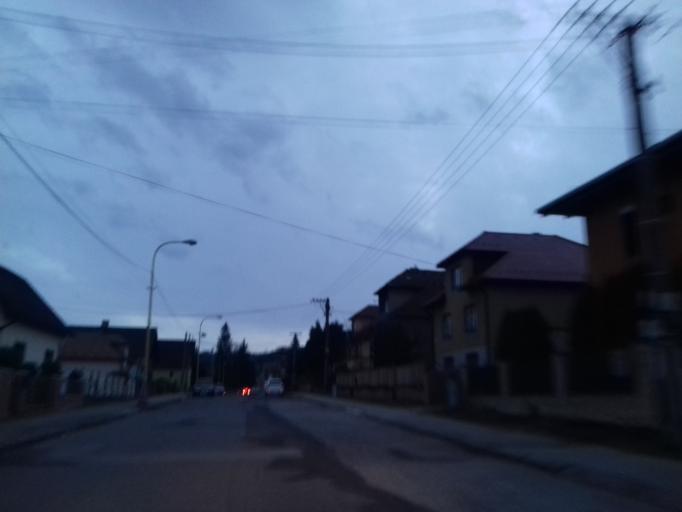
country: SK
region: Zilinsky
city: Ruzomberok
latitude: 49.0796
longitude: 19.2951
